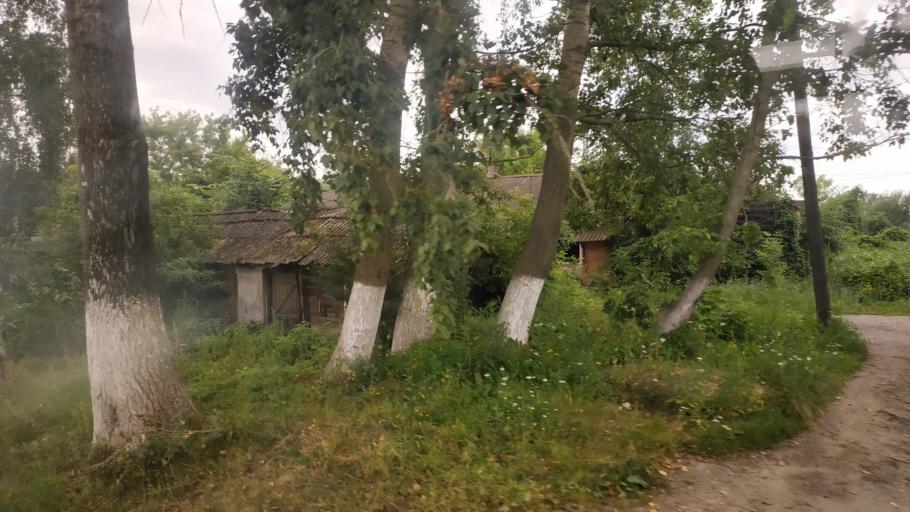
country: RU
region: Moskovskaya
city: Beloomut
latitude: 54.9153
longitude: 39.2611
